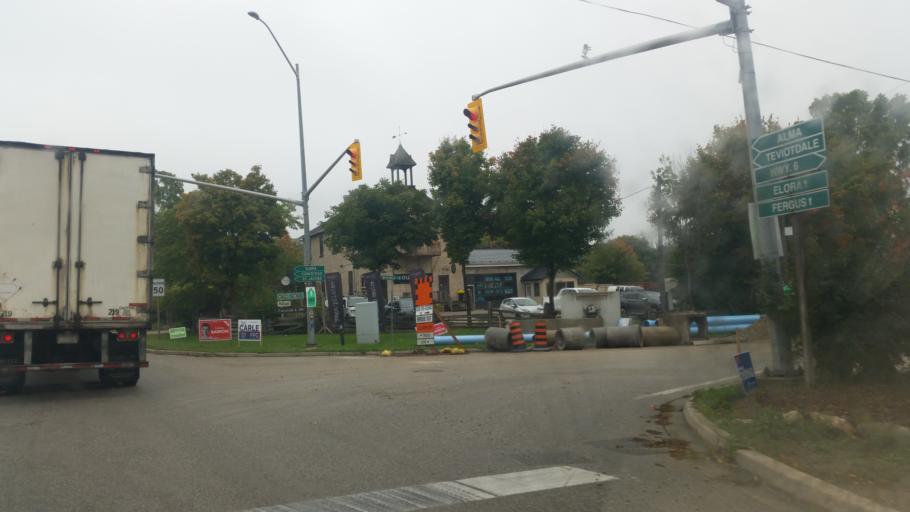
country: CA
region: Ontario
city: Waterloo
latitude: 43.6911
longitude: -80.4486
